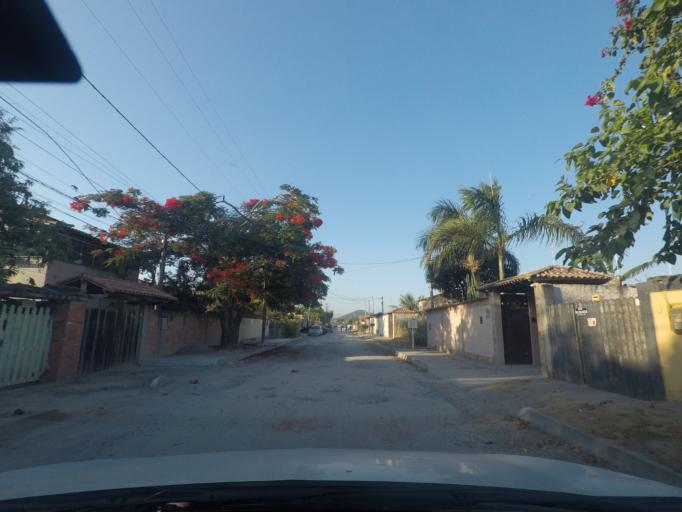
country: BR
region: Rio de Janeiro
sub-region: Marica
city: Marica
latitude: -22.9661
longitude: -42.9316
